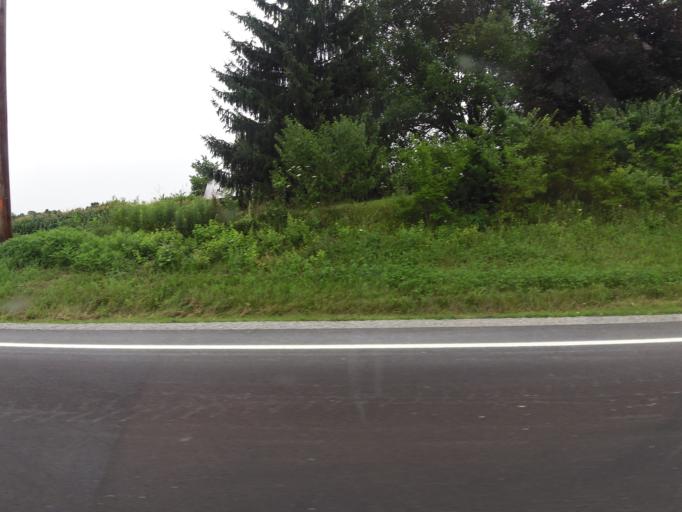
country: US
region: Ohio
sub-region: Clinton County
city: Blanchester
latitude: 39.2273
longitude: -83.9106
